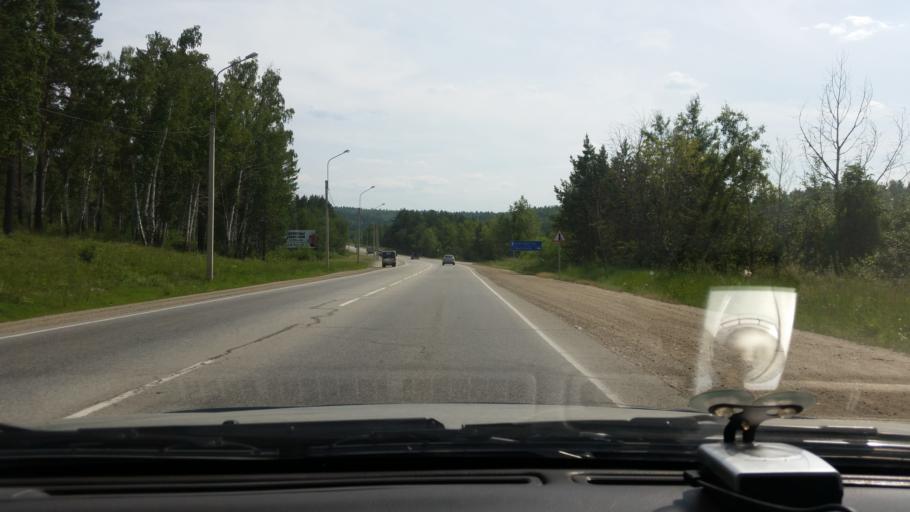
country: RU
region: Irkutsk
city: Smolenshchina
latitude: 52.2386
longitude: 104.1480
